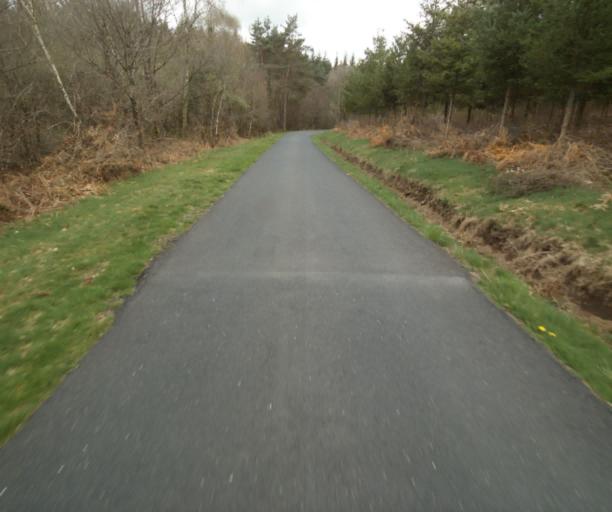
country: FR
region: Limousin
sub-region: Departement de la Correze
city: Correze
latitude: 45.3088
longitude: 1.8994
